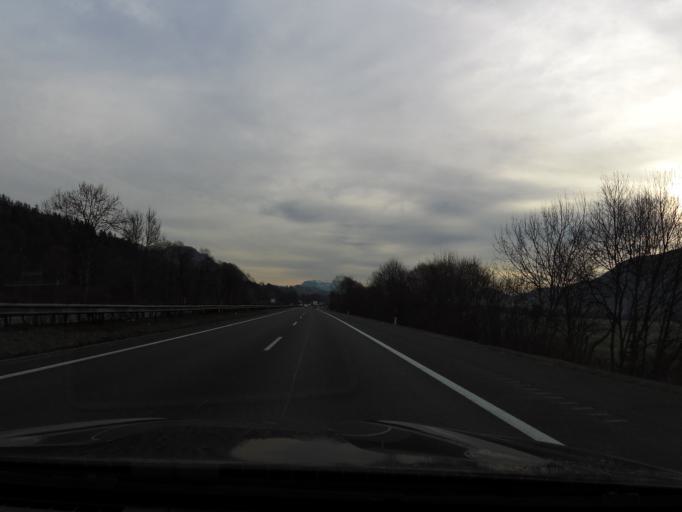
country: AT
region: Tyrol
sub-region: Politischer Bezirk Kufstein
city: Radfeld
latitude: 47.4622
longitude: 11.9390
